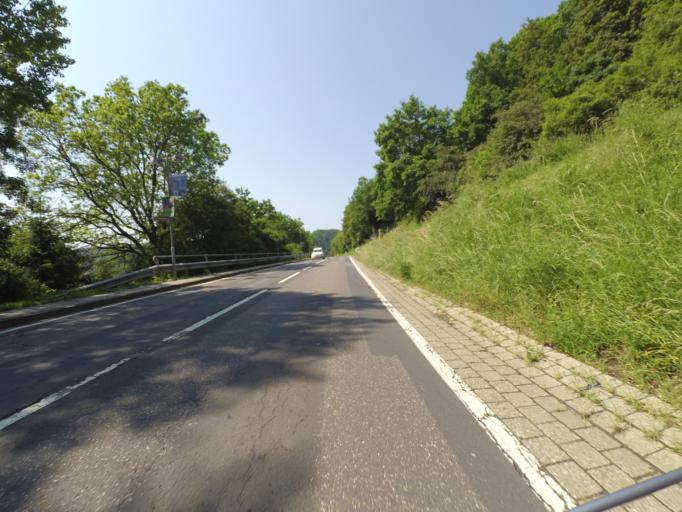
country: DE
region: Rheinland-Pfalz
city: Monreal
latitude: 50.3032
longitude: 7.1677
